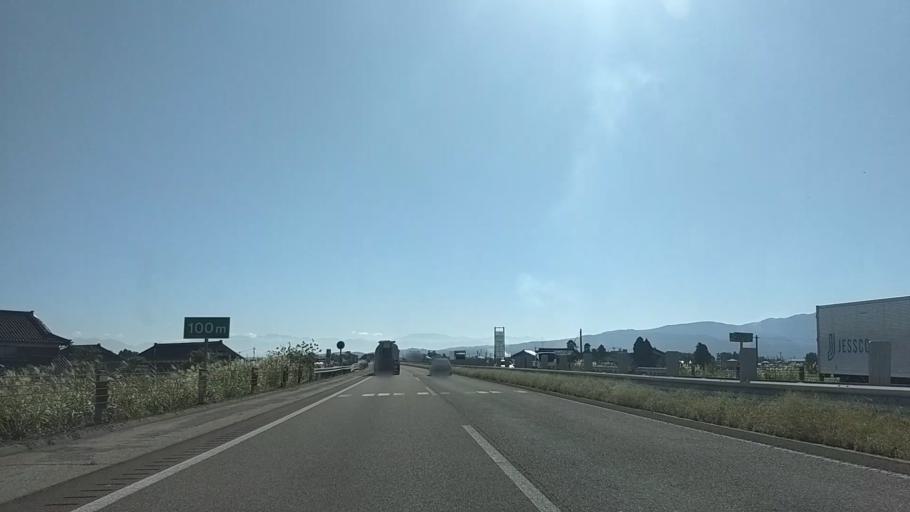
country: JP
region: Toyama
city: Nanto-shi
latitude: 36.6242
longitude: 136.9333
